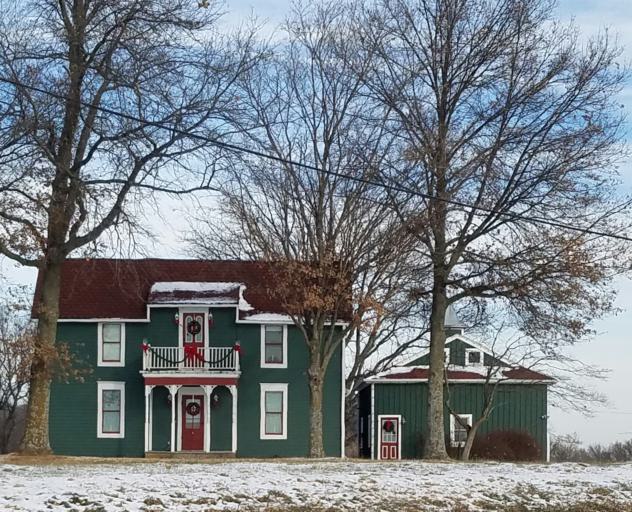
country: US
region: Missouri
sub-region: Ray County
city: Albany
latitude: 39.1229
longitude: -94.0870
